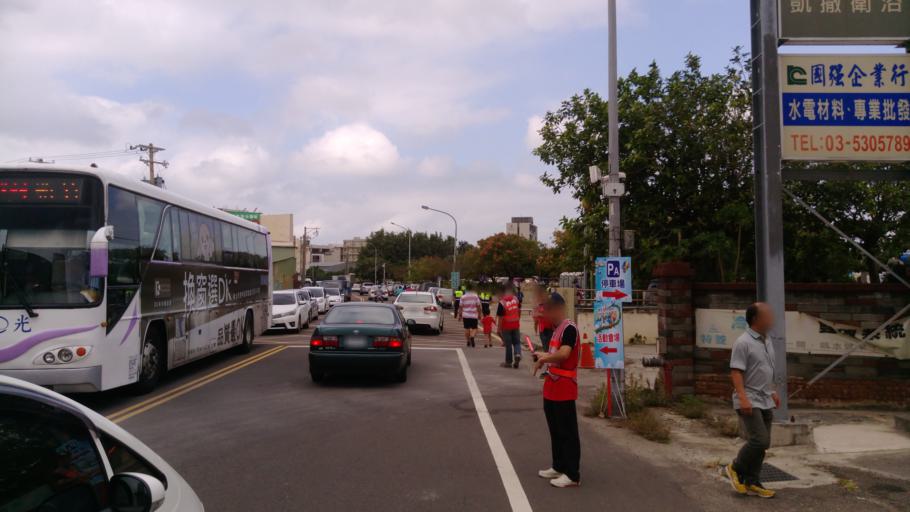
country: TW
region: Taiwan
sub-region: Hsinchu
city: Hsinchu
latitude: 24.7921
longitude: 120.9310
